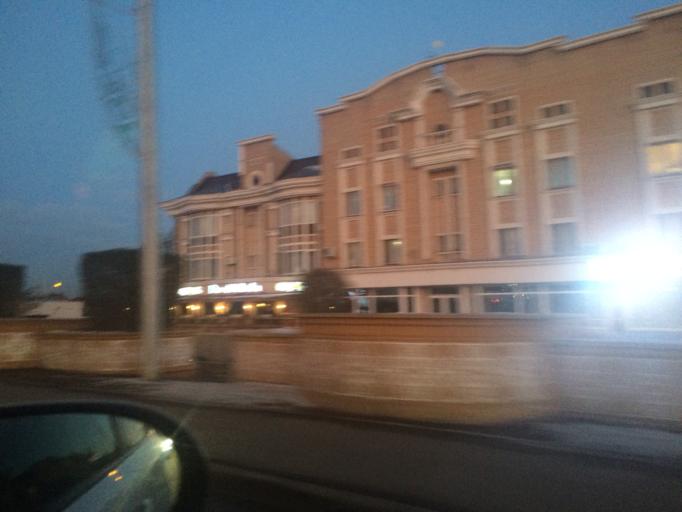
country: KZ
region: Astana Qalasy
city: Astana
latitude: 51.1394
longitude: 71.4177
